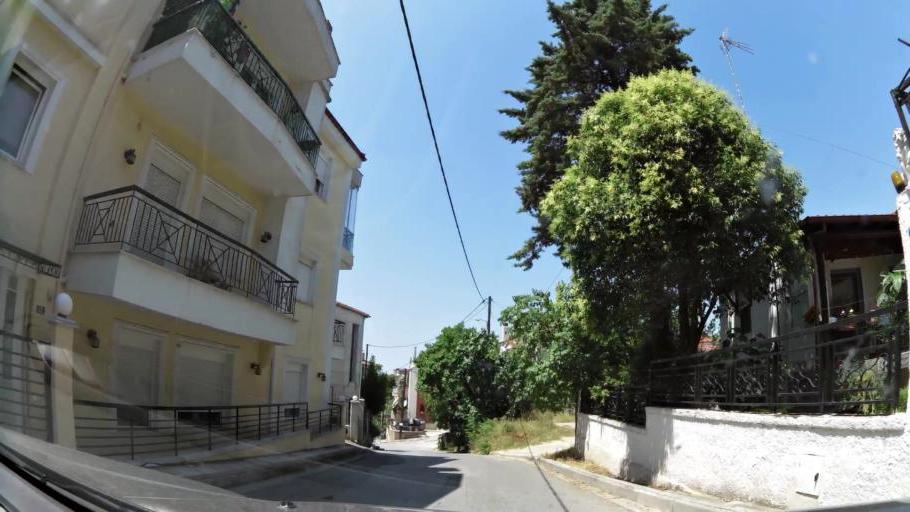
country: GR
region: Central Macedonia
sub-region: Nomos Thessalonikis
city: Trilofos
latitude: 40.4666
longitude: 22.9708
